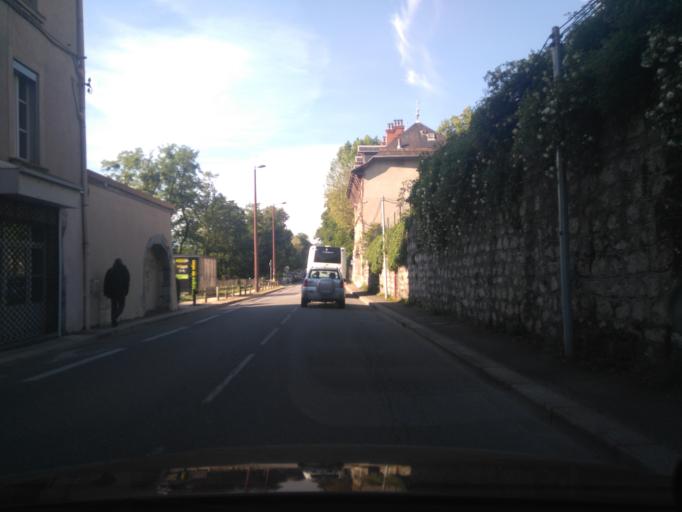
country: FR
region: Rhone-Alpes
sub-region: Departement de l'Isere
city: La Tronche
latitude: 45.2017
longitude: 5.7341
